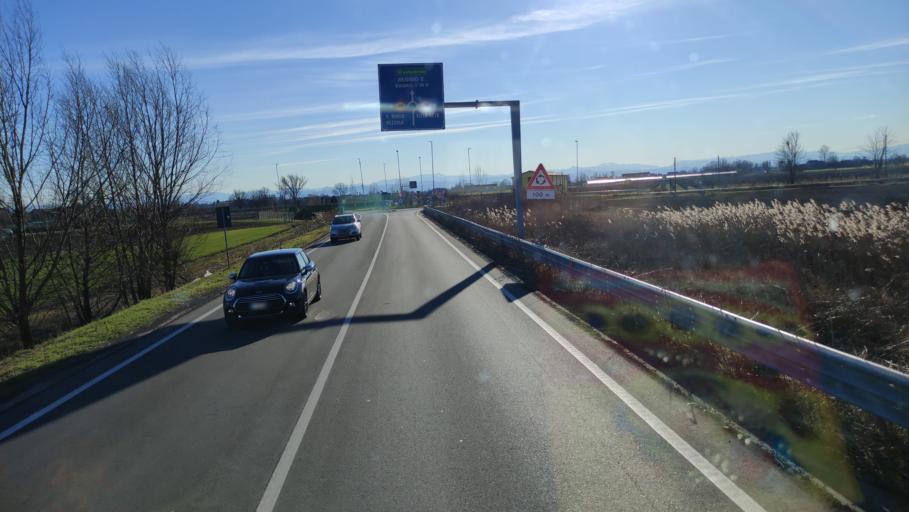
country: IT
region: Emilia-Romagna
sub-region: Provincia di Reggio Emilia
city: Bagnolo in Piano
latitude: 44.8097
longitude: 10.6871
